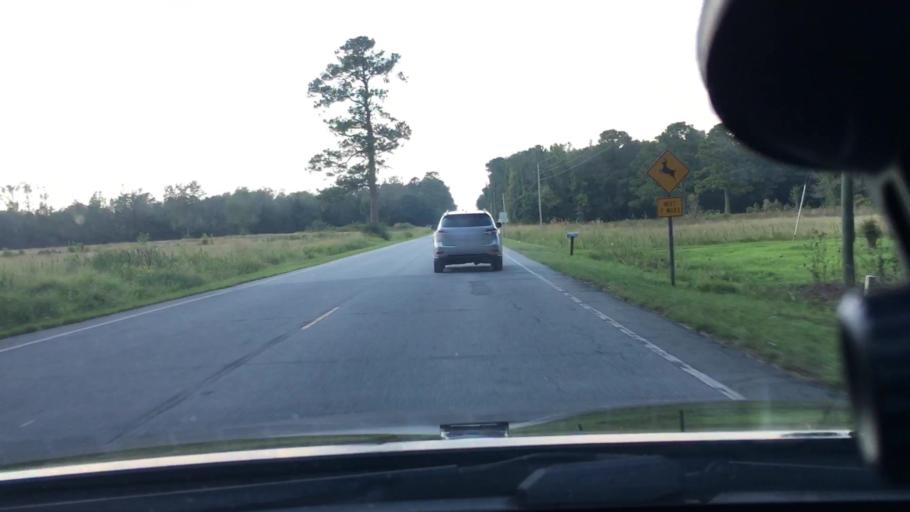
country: US
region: North Carolina
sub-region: Craven County
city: Vanceboro
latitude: 35.3927
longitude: -77.2321
